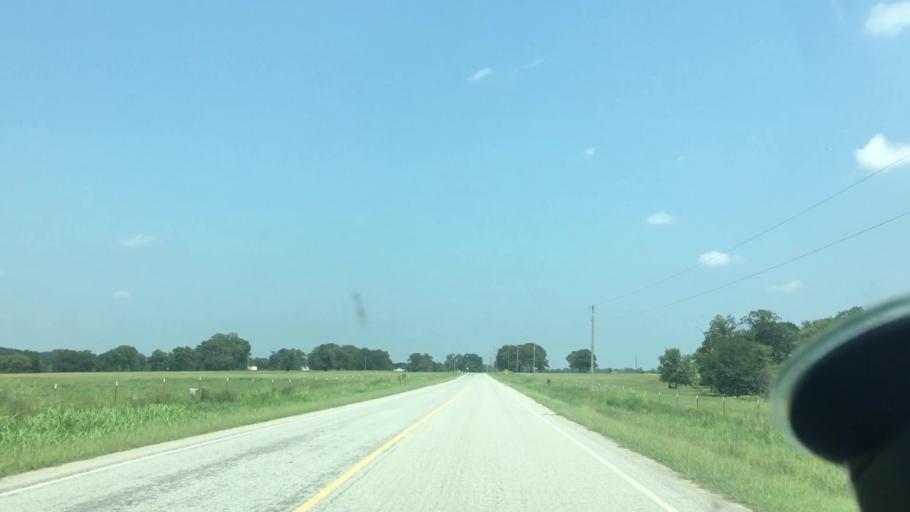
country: US
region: Oklahoma
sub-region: Atoka County
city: Atoka
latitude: 34.2740
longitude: -95.9361
